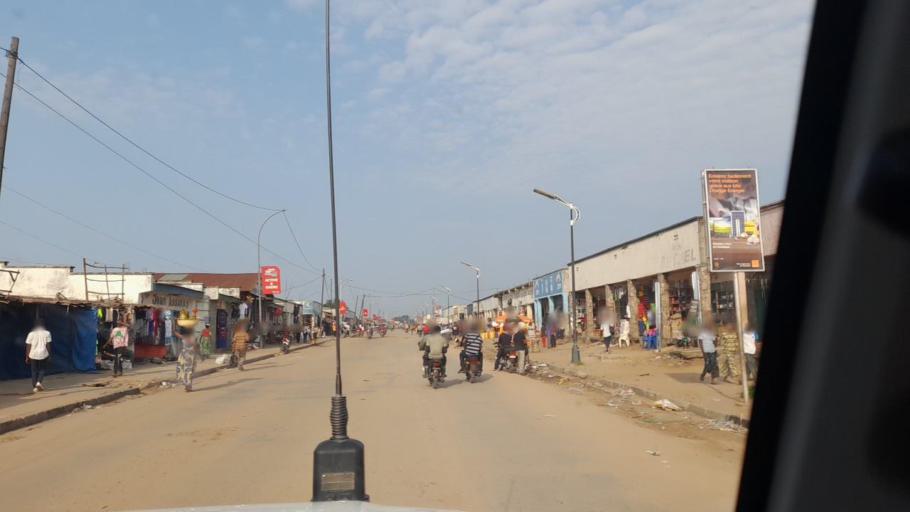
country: CD
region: Kasai-Occidental
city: Kananga
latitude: -5.8946
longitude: 22.3991
